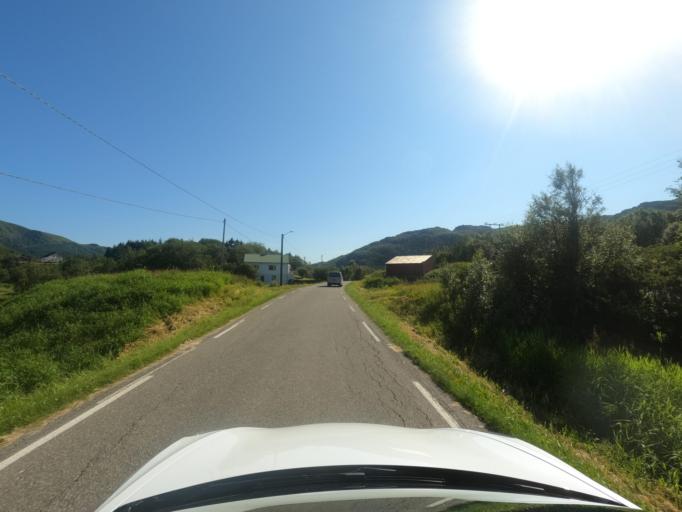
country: NO
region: Nordland
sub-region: Hadsel
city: Stokmarknes
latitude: 68.3024
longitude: 15.0190
